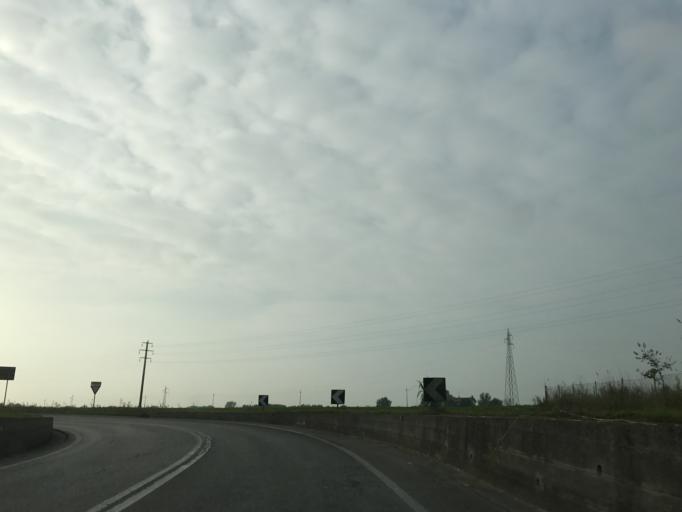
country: IT
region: Emilia-Romagna
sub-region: Forli-Cesena
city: Cesenatico
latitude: 44.1919
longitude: 12.3992
